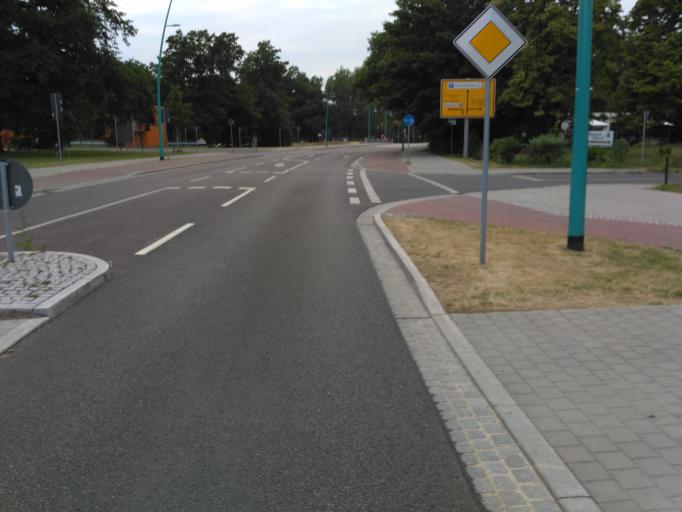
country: DE
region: Saxony
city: Hoyerswerda
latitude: 51.4388
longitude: 14.2558
